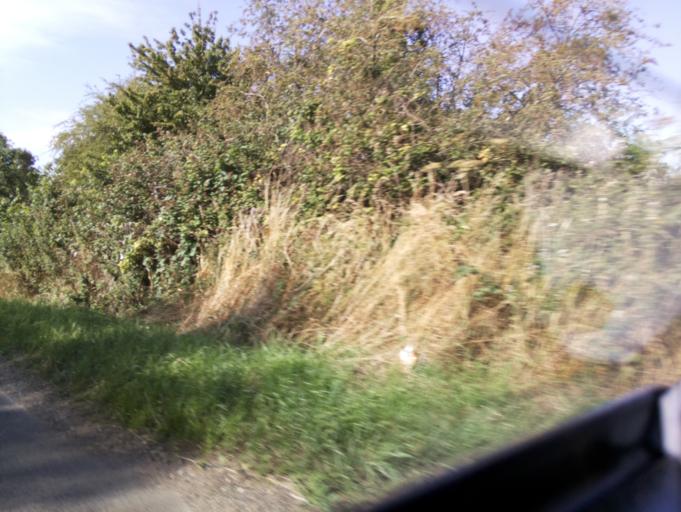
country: GB
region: England
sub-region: Oxfordshire
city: Faringdon
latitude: 51.7011
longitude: -1.5910
